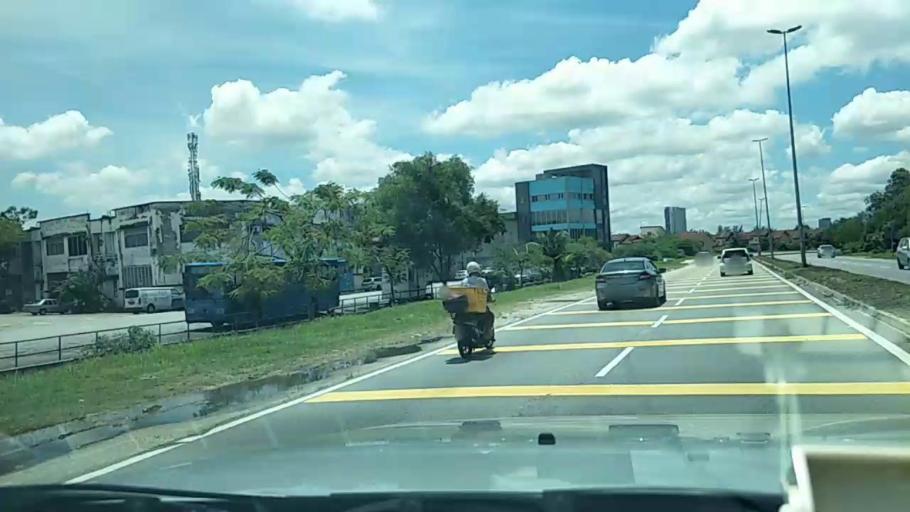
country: MY
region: Selangor
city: Subang Jaya
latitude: 2.9733
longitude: 101.6122
